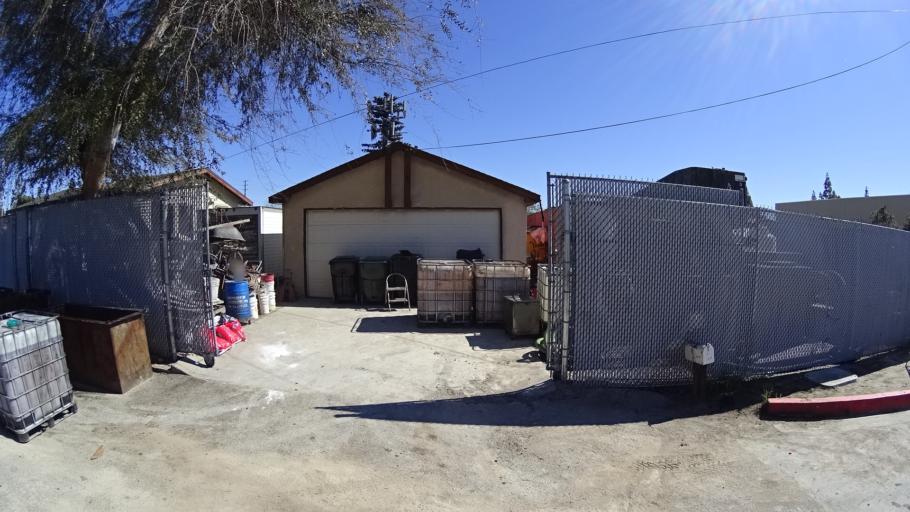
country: US
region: California
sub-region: Orange County
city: Yorba Linda
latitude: 33.8666
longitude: -117.8234
